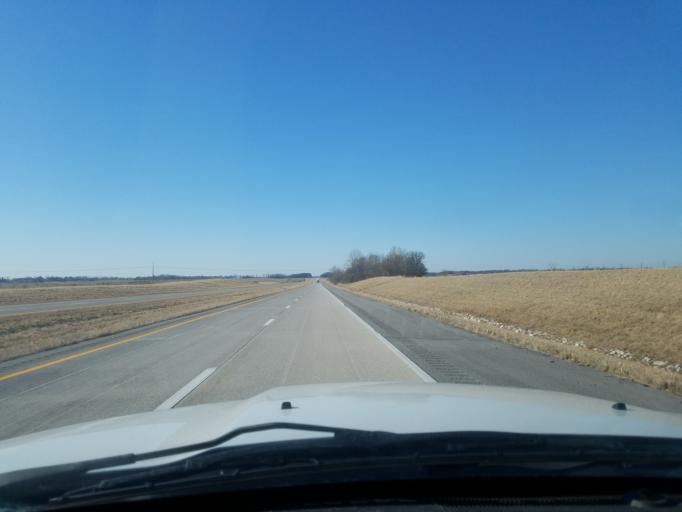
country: US
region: Kentucky
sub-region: Henderson County
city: Henderson
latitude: 37.7976
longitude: -87.5058
